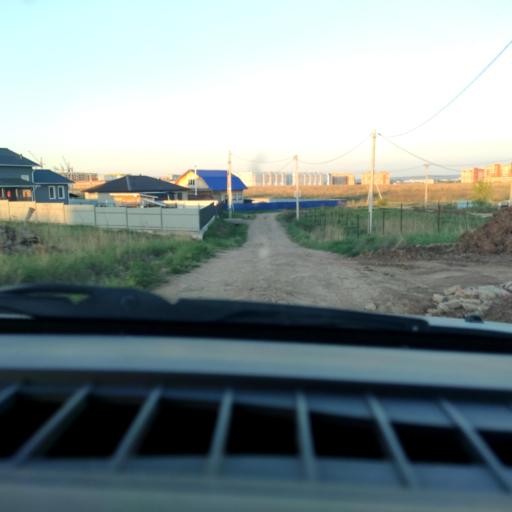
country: RU
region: Perm
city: Froly
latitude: 57.9282
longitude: 56.2865
